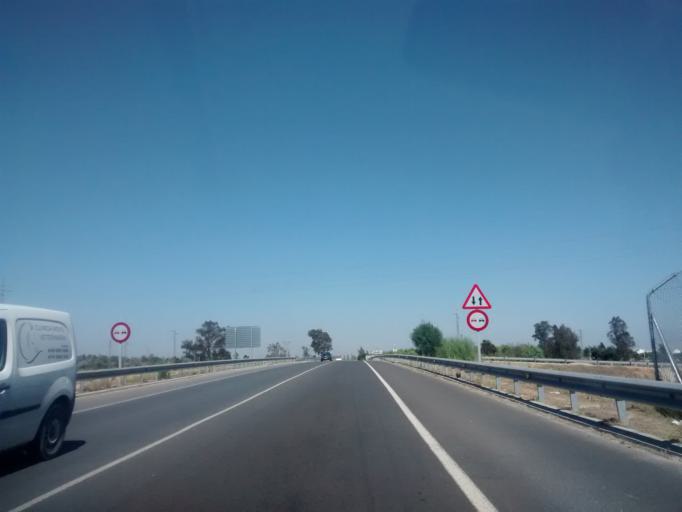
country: ES
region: Andalusia
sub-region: Provincia de Huelva
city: Almonte
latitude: 37.1404
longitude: -6.4963
